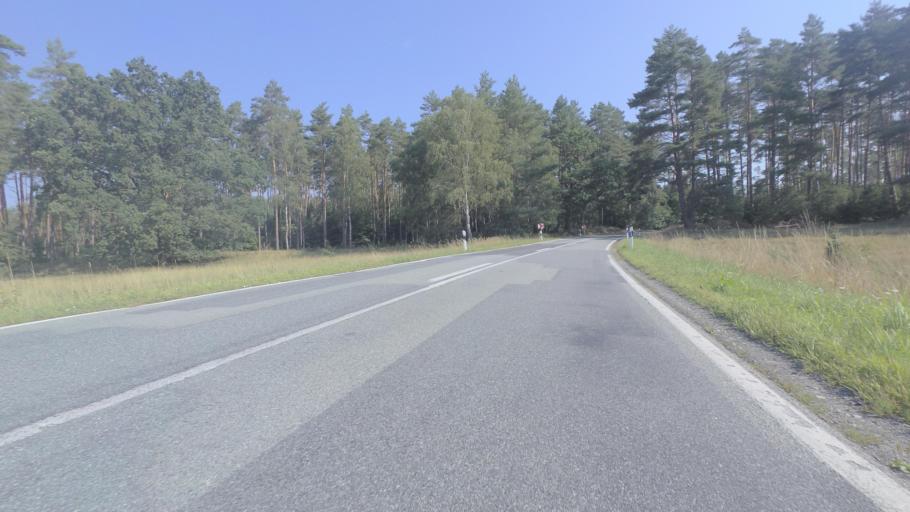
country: DE
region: Mecklenburg-Vorpommern
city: Malchow
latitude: 53.5455
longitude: 12.4347
